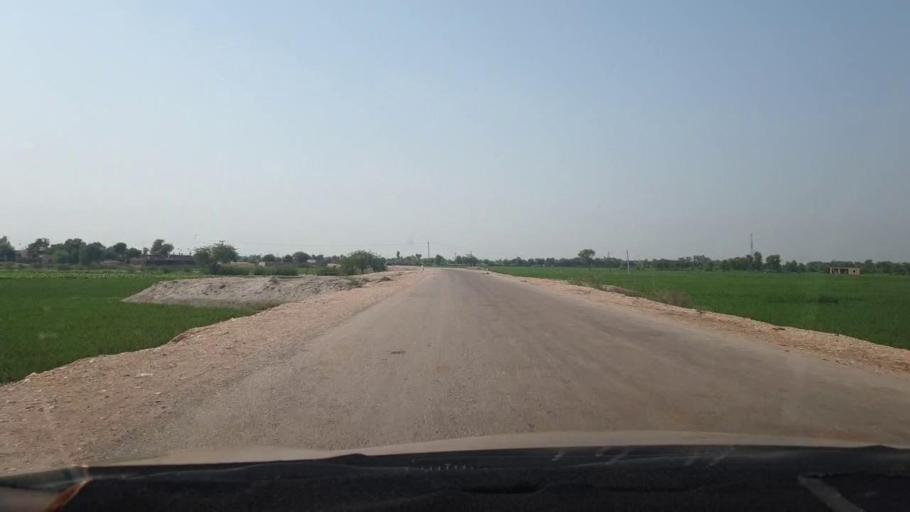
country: PK
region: Sindh
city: Larkana
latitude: 27.6083
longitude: 68.2391
